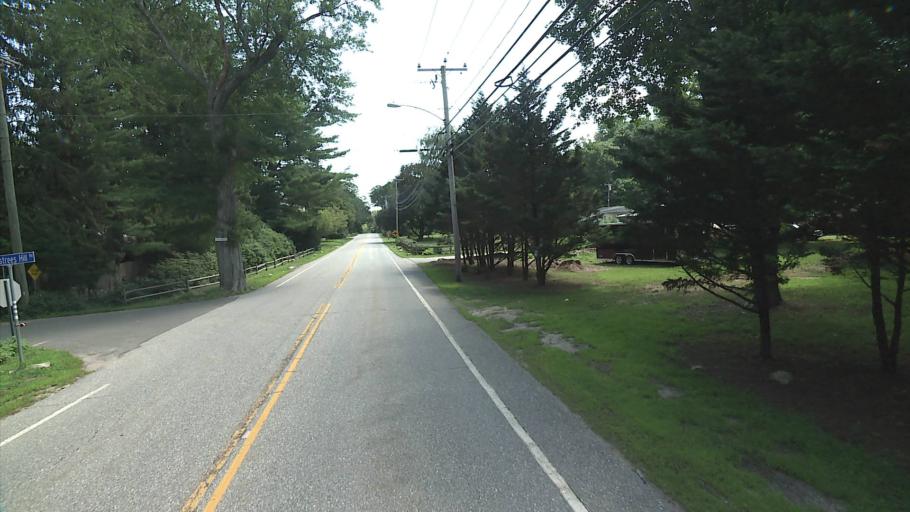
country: US
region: Connecticut
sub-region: Middlesex County
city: Essex Village
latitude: 41.3417
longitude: -72.3908
